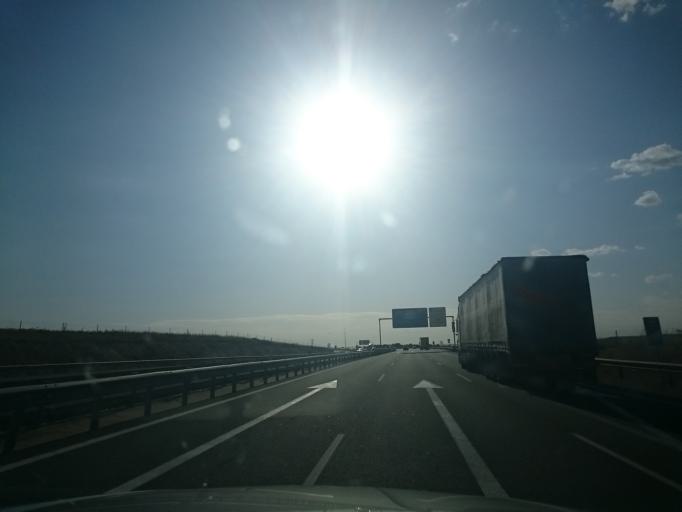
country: ES
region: Castille and Leon
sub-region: Provincia de Burgos
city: Cardenadijo
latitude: 42.3253
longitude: -3.6674
